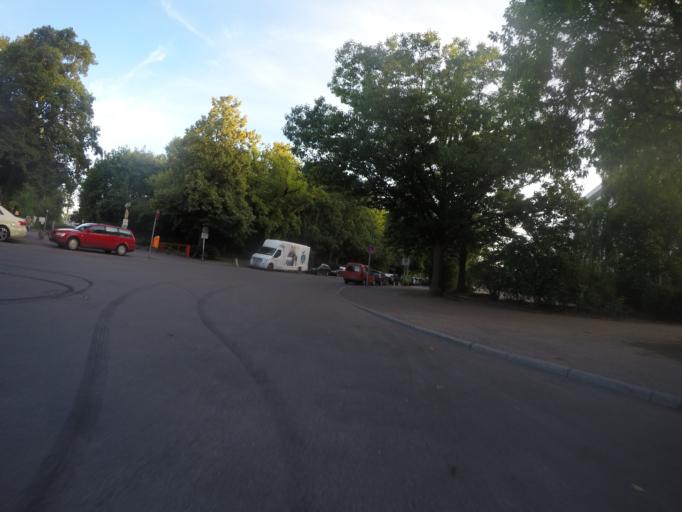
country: DE
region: Berlin
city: Halensee
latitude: 52.4860
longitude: 13.3007
